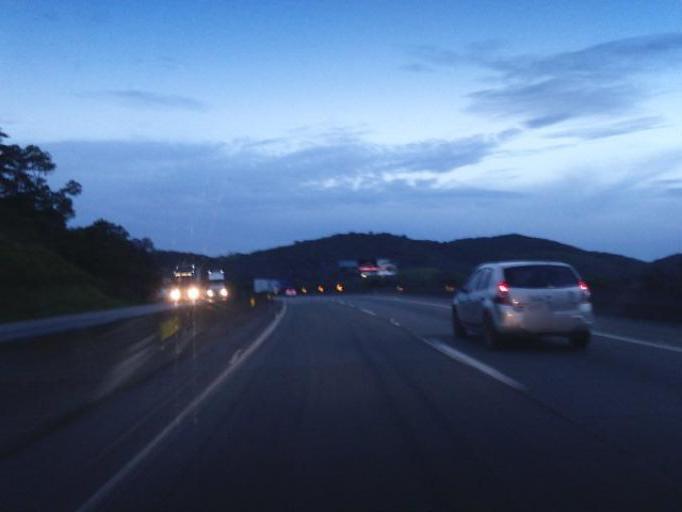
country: BR
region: Santa Catarina
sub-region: Joinville
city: Joinville
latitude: -26.4320
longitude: -48.8227
